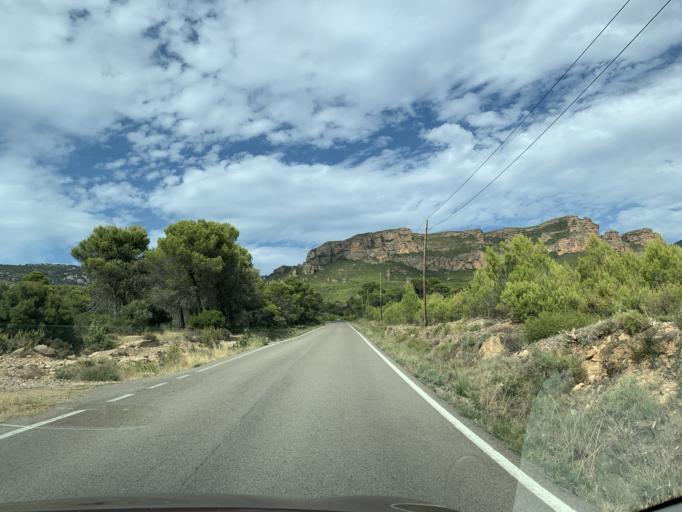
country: ES
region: Aragon
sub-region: Provincia de Zaragoza
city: Santa Eulalia de Gallego
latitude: 42.3251
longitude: -0.7238
